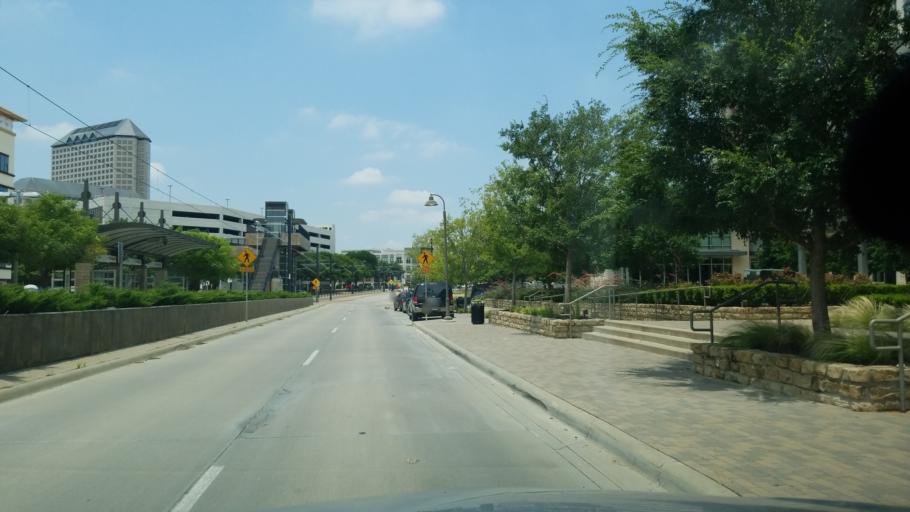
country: US
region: Texas
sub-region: Dallas County
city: Irving
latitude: 32.8686
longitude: -96.9334
